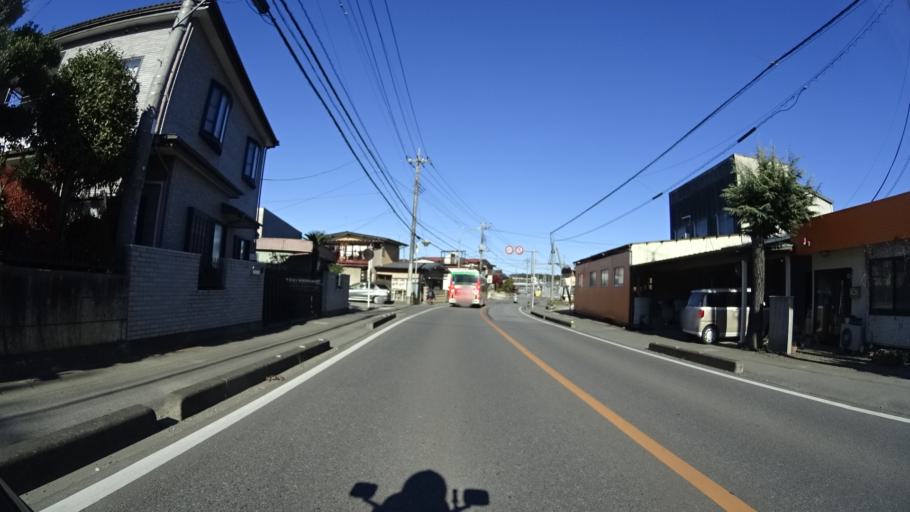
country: JP
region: Tochigi
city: Kanuma
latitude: 36.5784
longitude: 139.7647
